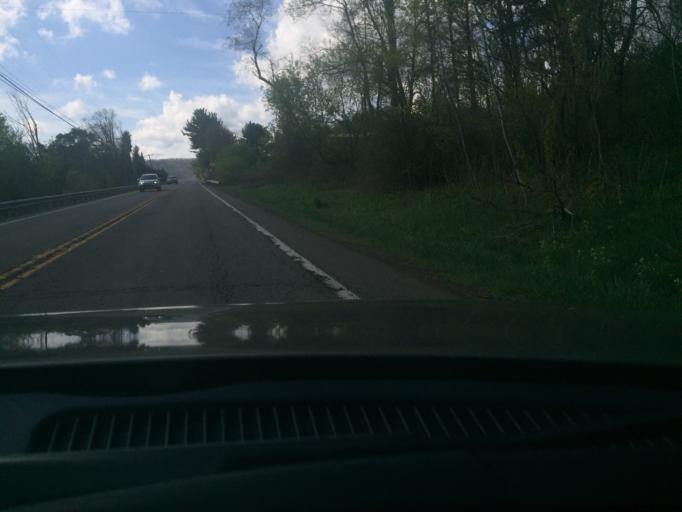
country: US
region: Pennsylvania
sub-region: Luzerne County
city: Conyngham
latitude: 41.0069
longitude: -76.0759
